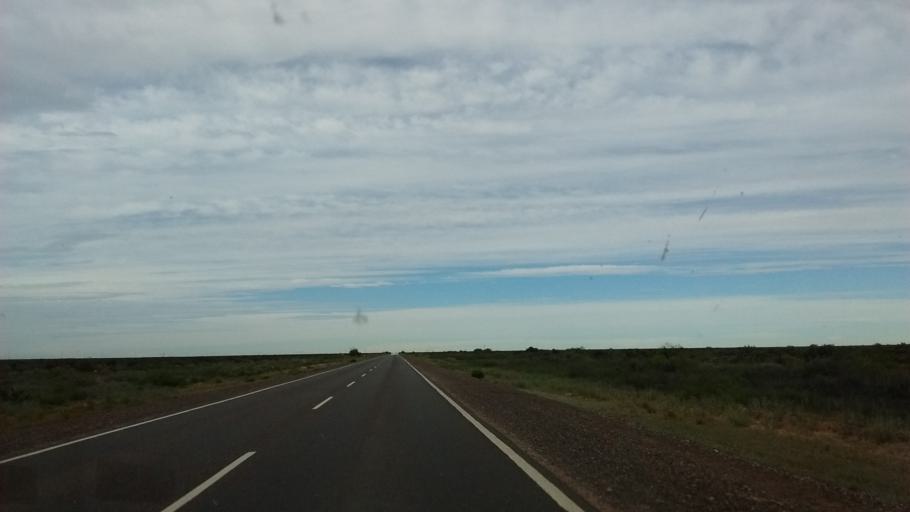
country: AR
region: Rio Negro
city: Contraalmirante Cordero
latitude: -38.5090
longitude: -68.0677
